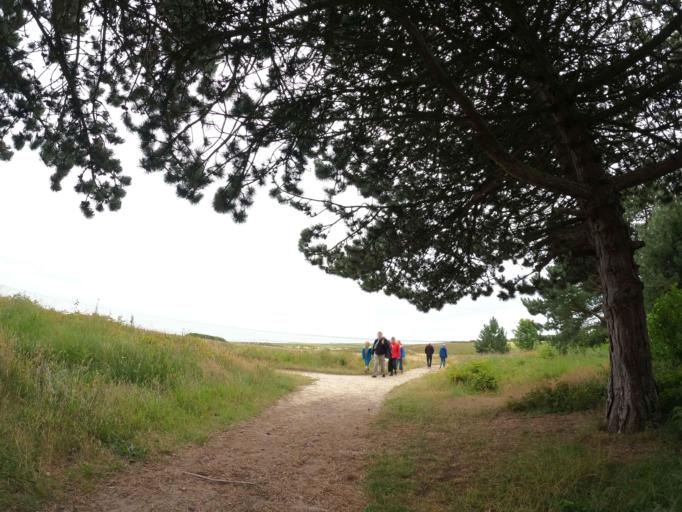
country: DE
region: Schleswig-Holstein
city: Tinnum
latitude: 54.9521
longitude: 8.3536
